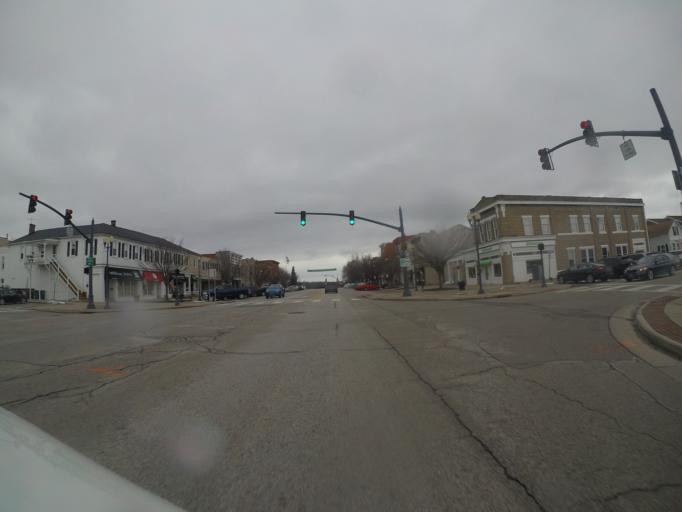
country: US
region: Ohio
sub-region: Wood County
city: Perrysburg
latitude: 41.5592
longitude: -83.6292
